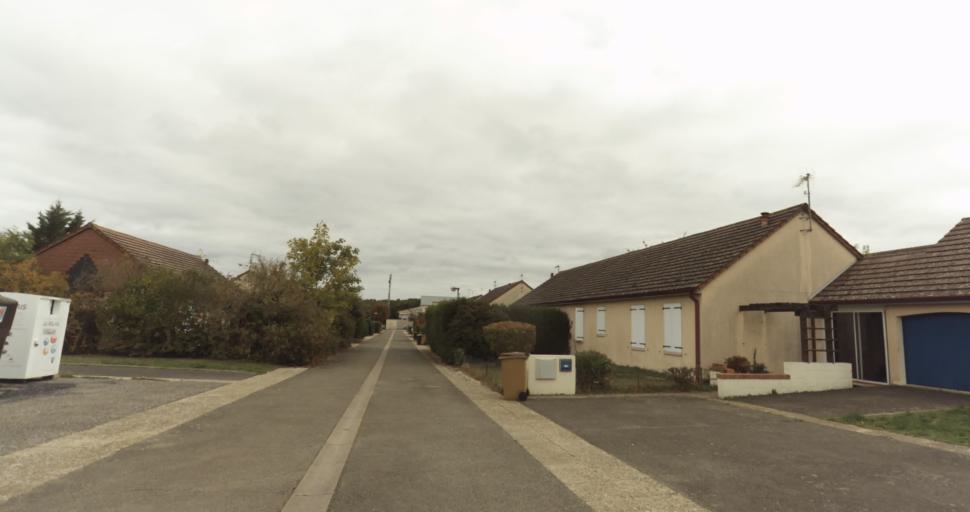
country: FR
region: Centre
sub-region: Departement d'Eure-et-Loir
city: Garnay
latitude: 48.7283
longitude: 1.3392
